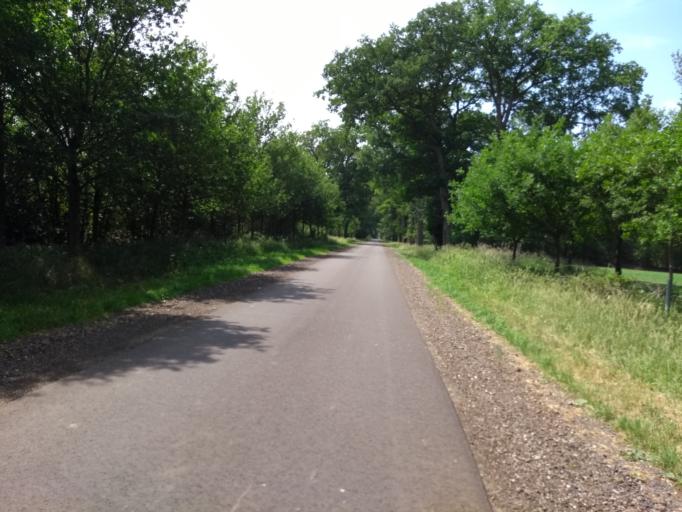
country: NL
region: Overijssel
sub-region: Gemeente Almelo
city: Almelo
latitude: 52.3620
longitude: 6.6939
